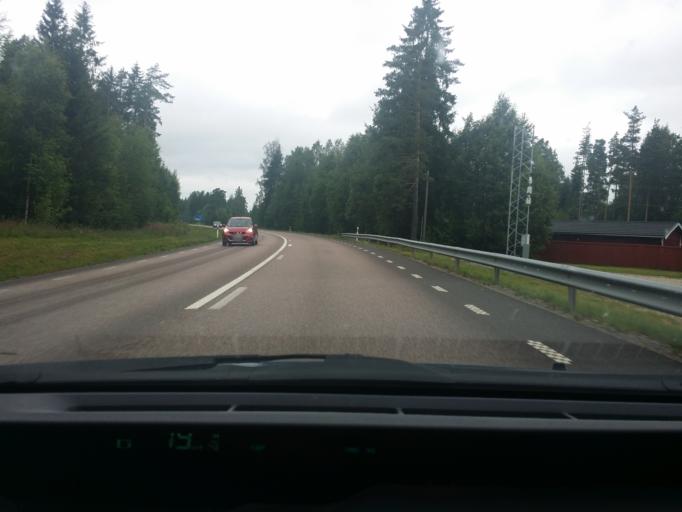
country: SE
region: Dalarna
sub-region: Borlange Kommun
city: Borlaenge
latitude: 60.5280
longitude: 15.3456
